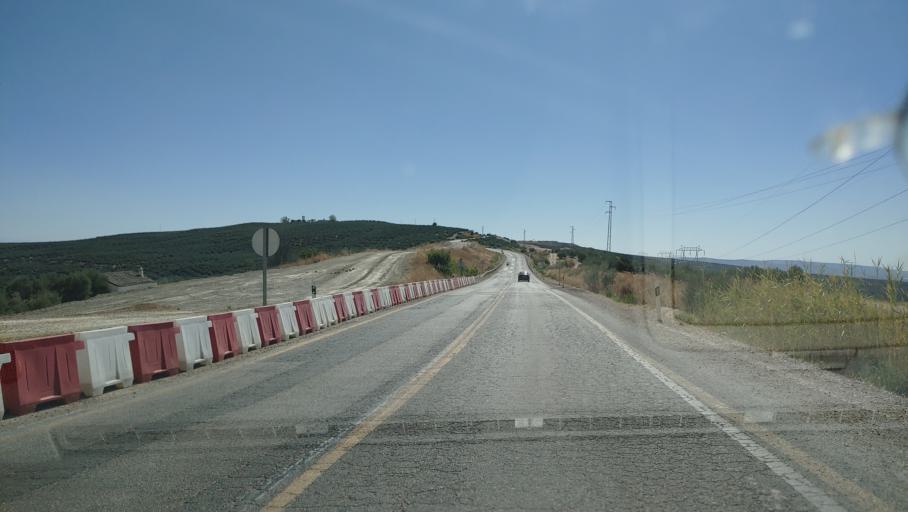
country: ES
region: Andalusia
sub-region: Provincia de Jaen
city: Iznatoraf
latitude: 38.1394
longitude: -3.0457
